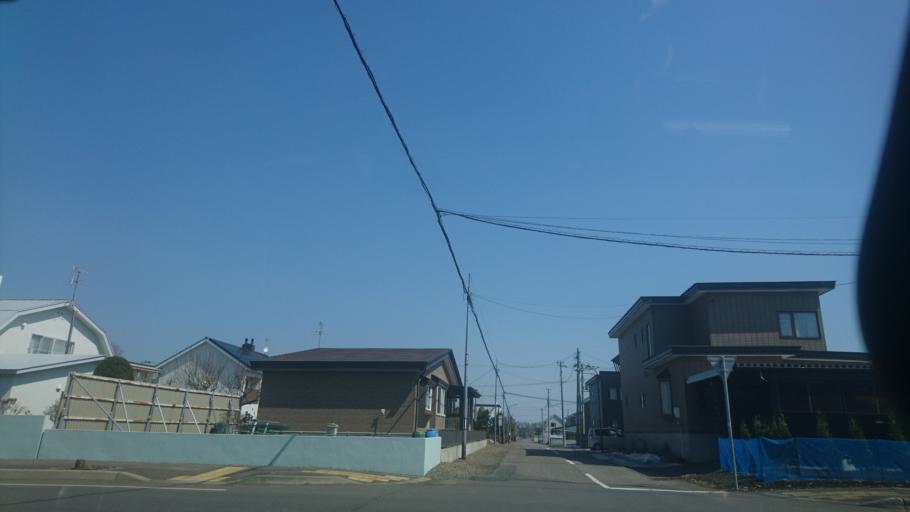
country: JP
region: Hokkaido
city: Obihiro
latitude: 42.9125
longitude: 143.0563
